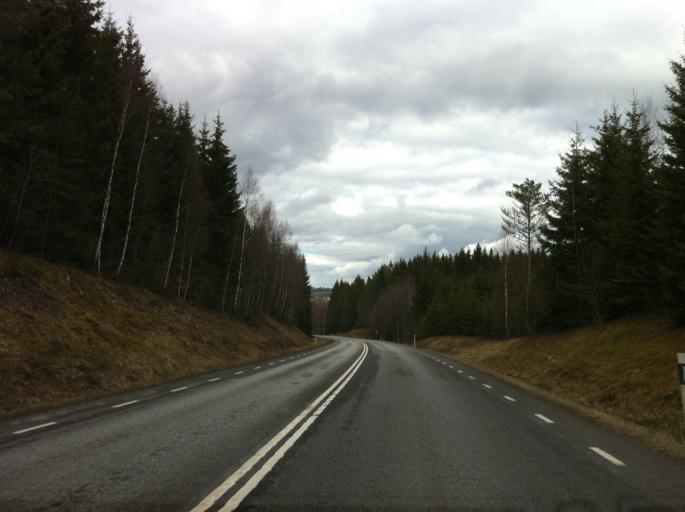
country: SE
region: Vaestra Goetaland
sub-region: Tranemo Kommun
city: Limmared
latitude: 57.5917
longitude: 13.4192
